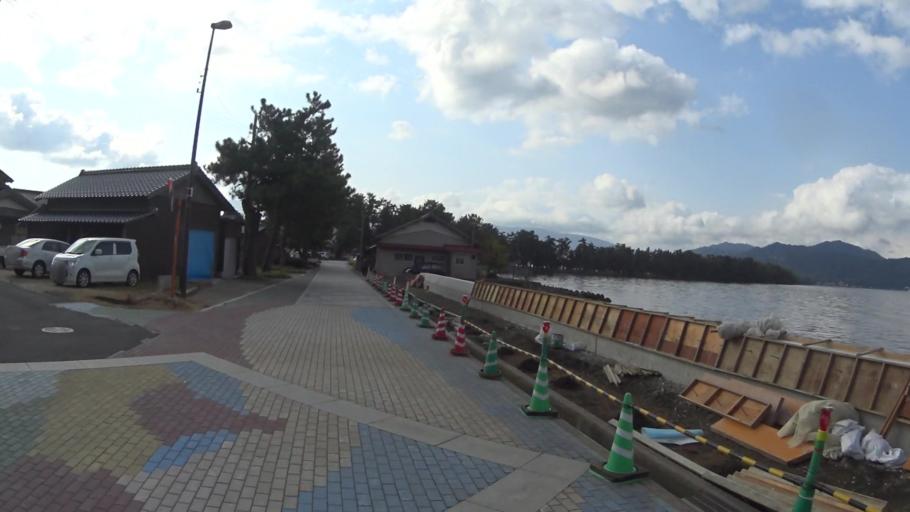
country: JP
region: Kyoto
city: Miyazu
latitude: 35.5795
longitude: 135.1975
